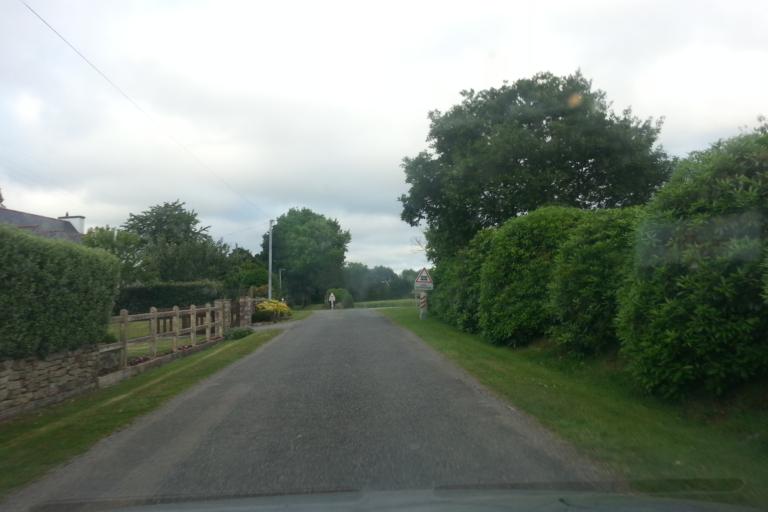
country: FR
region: Brittany
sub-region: Departement du Finistere
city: Mellac
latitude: 47.8862
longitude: -3.5909
